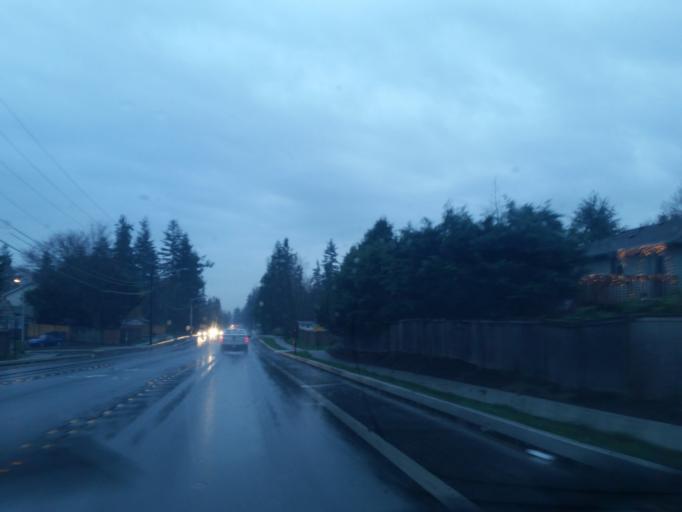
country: US
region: Washington
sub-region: Snohomish County
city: Meadowdale
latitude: 47.8572
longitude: -122.3037
